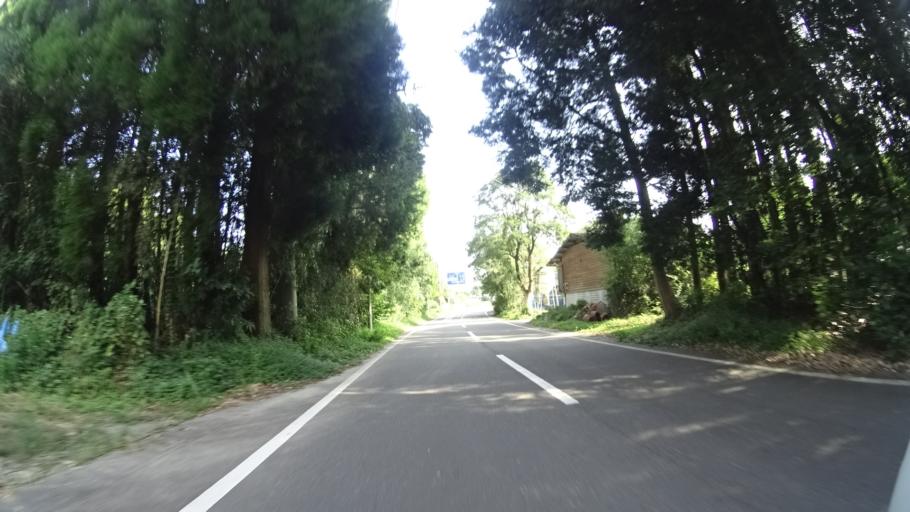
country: JP
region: Kagoshima
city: Okuchi-shinohara
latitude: 32.0151
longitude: 130.5773
